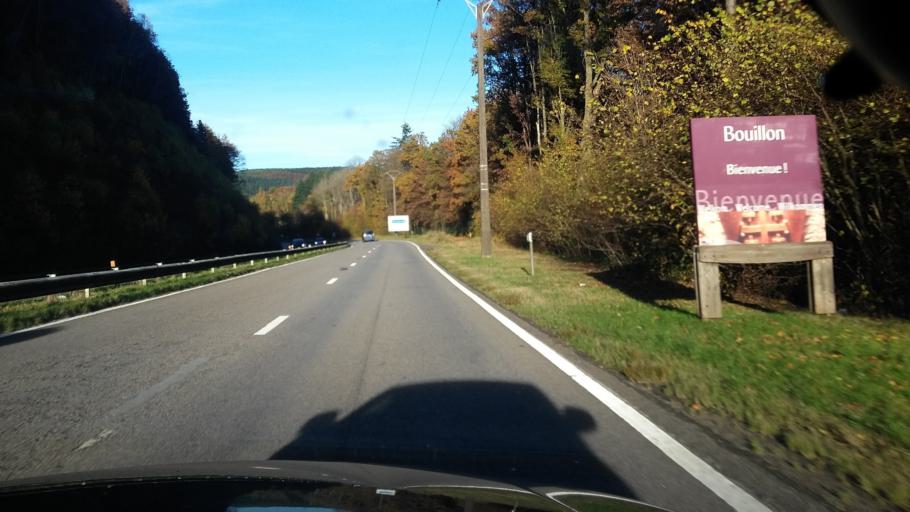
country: BE
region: Wallonia
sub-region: Province du Luxembourg
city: Bouillon
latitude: 49.7773
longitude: 5.0773
